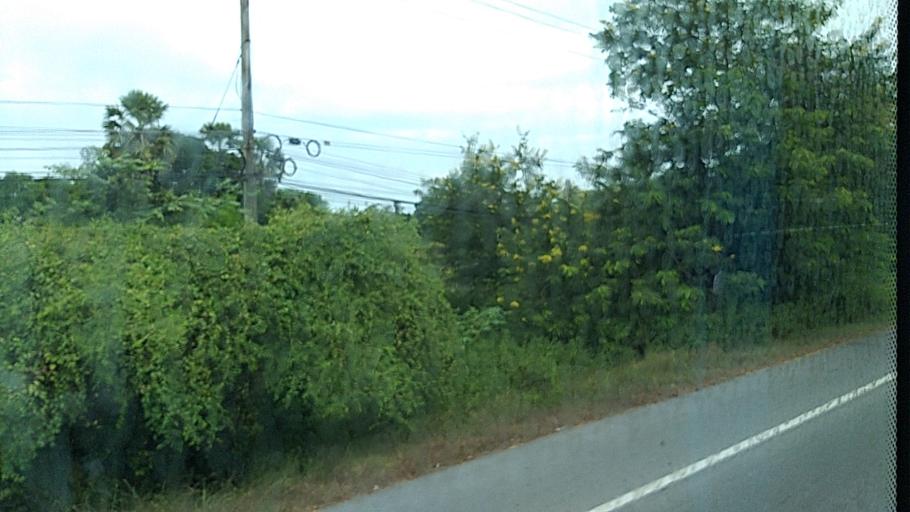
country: TH
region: Roi Et
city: Changhan
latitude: 16.1114
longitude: 103.5046
